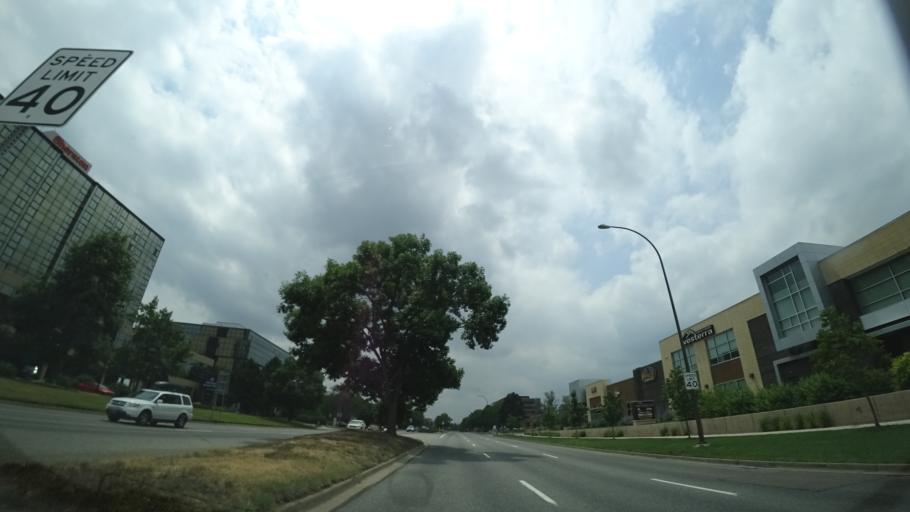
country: US
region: Colorado
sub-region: Jefferson County
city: Applewood
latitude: 39.7222
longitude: -105.1325
